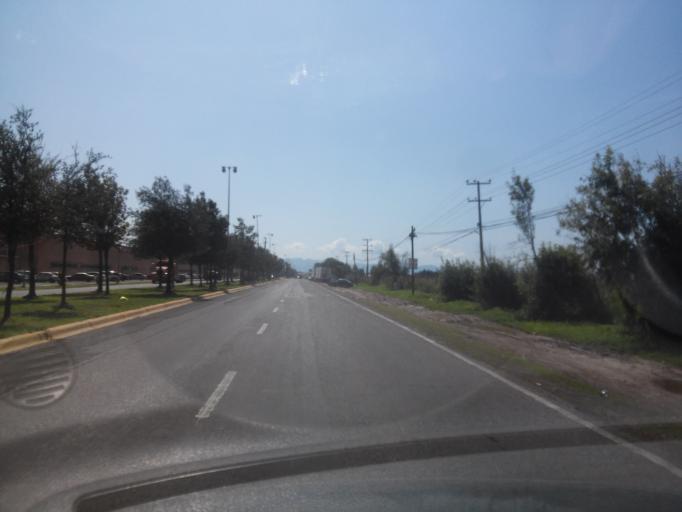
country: MX
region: Durango
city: Victoria de Durango
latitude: 23.9935
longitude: -104.6300
